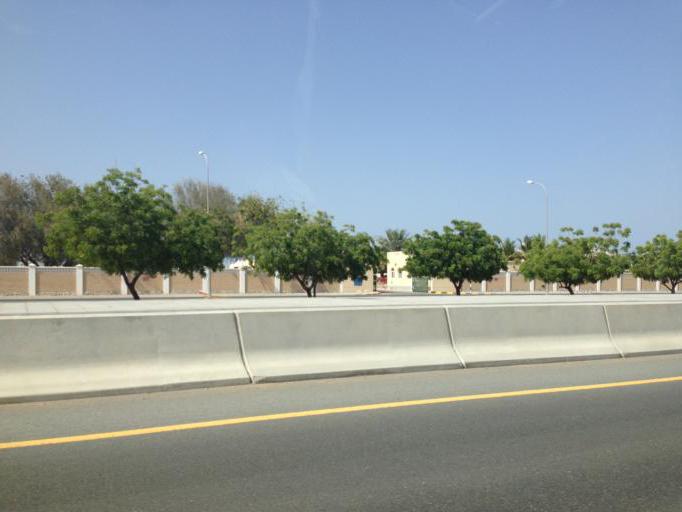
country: OM
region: Muhafazat Masqat
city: Bawshar
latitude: 23.6038
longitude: 58.3329
